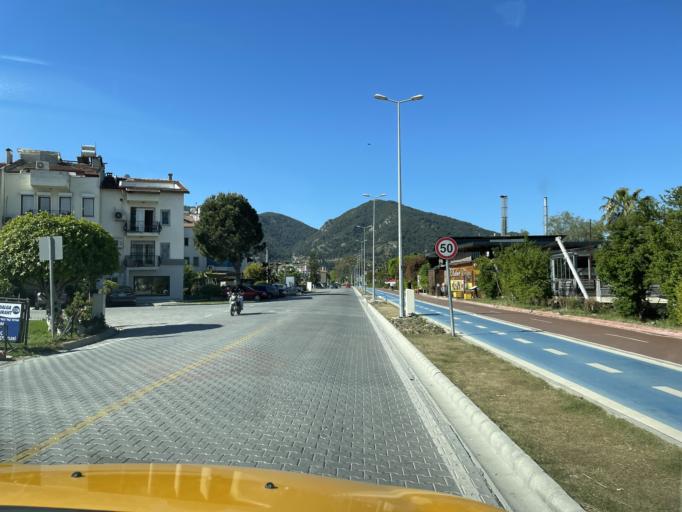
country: TR
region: Mugla
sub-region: Fethiye
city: Fethiye
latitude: 36.6330
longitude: 29.1199
